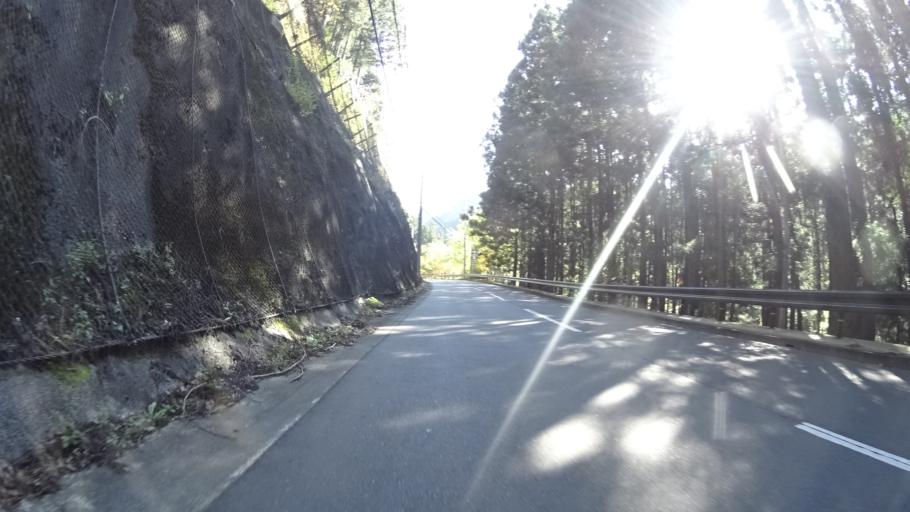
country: JP
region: Yamanashi
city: Uenohara
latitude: 35.7049
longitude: 139.1012
